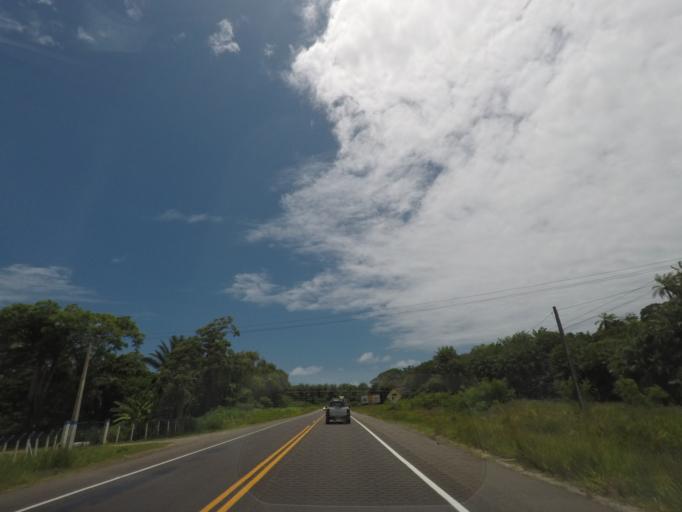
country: BR
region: Bahia
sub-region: Itaparica
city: Itaparica
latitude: -12.9812
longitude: -38.6322
